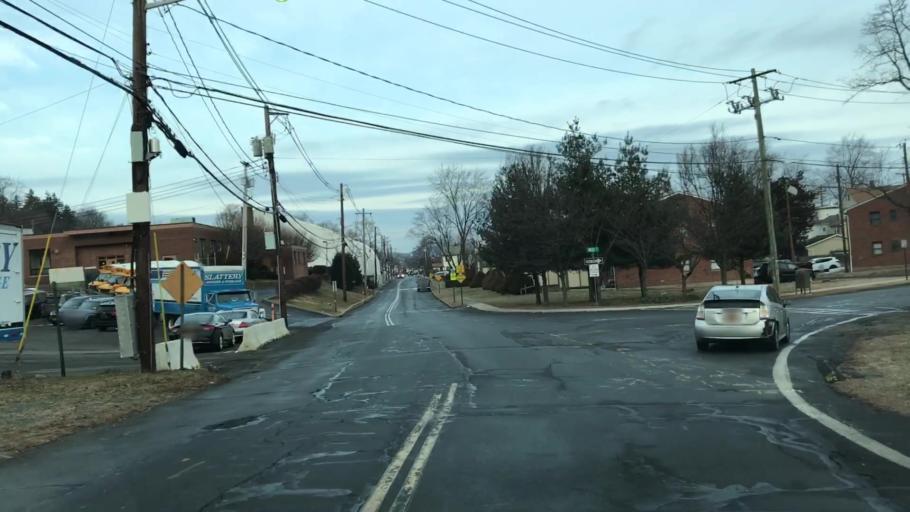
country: US
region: New York
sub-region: Rockland County
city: Haverstraw
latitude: 41.1918
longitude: -73.9606
